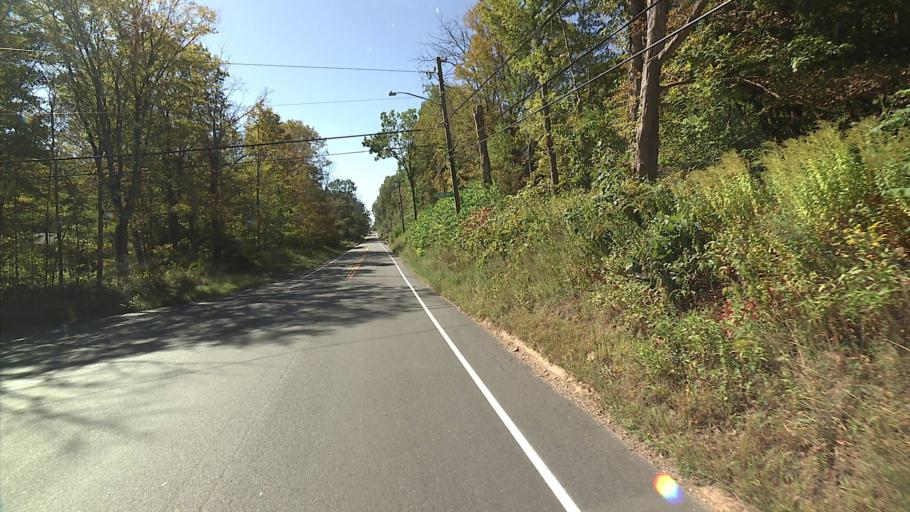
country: US
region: Connecticut
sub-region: New Haven County
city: Prospect
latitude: 41.4461
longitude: -72.9706
